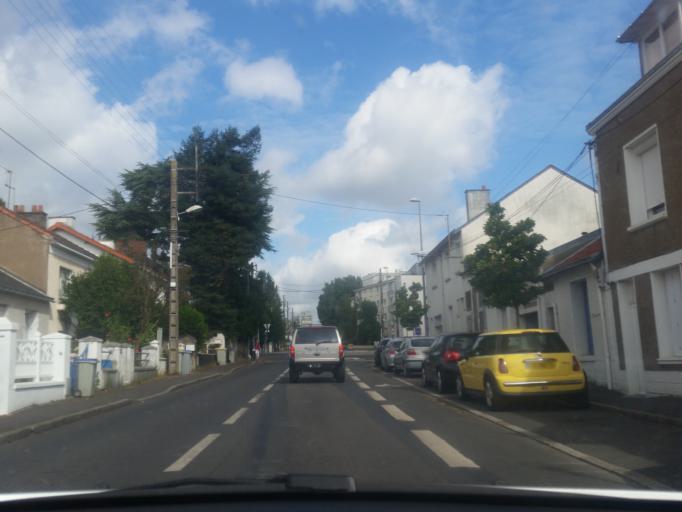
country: FR
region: Pays de la Loire
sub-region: Departement de la Loire-Atlantique
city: Nantes
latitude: 47.2369
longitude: -1.5242
